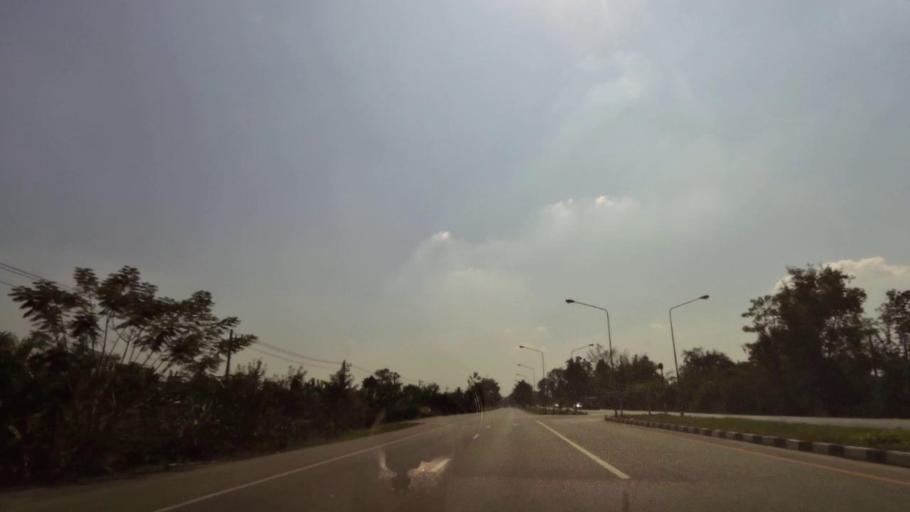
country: TH
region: Phichit
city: Bueng Na Rang
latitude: 16.2431
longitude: 100.1253
